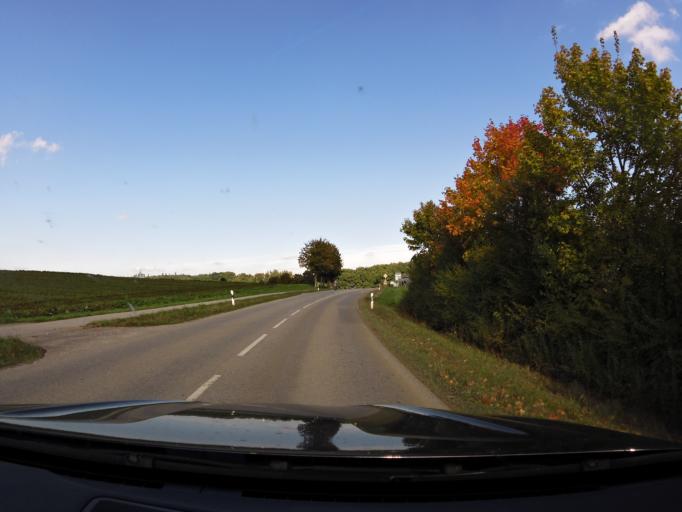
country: DE
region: Bavaria
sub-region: Lower Bavaria
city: Tiefenbach
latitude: 48.4939
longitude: 12.1013
